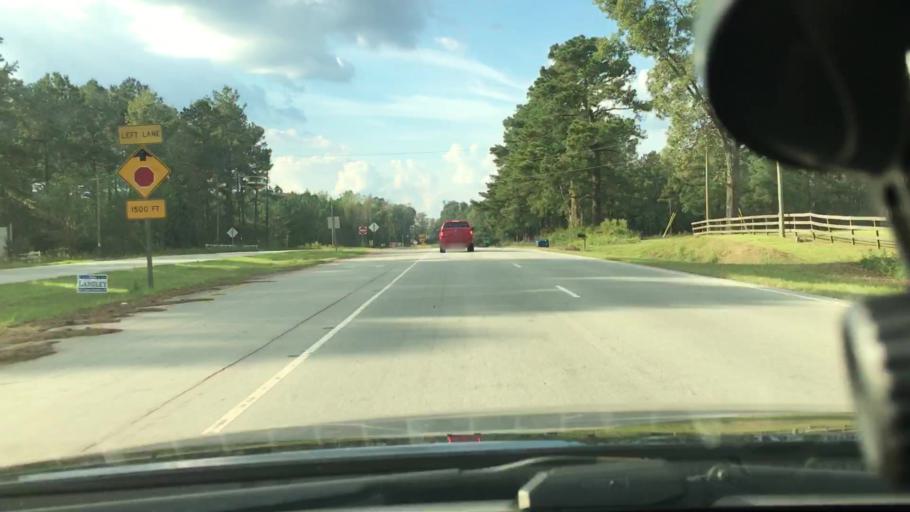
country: US
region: North Carolina
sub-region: Craven County
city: Vanceboro
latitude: 35.2848
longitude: -77.1262
